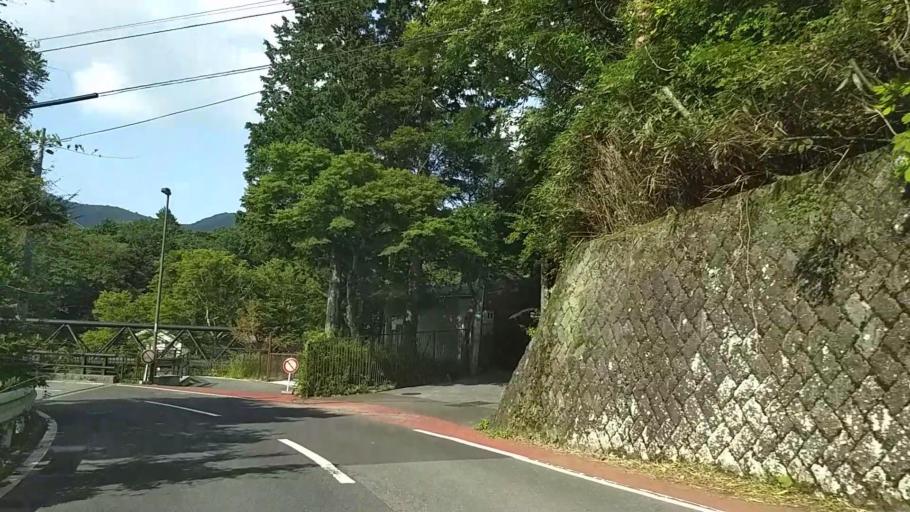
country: JP
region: Kanagawa
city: Hakone
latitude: 35.2650
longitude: 139.0158
